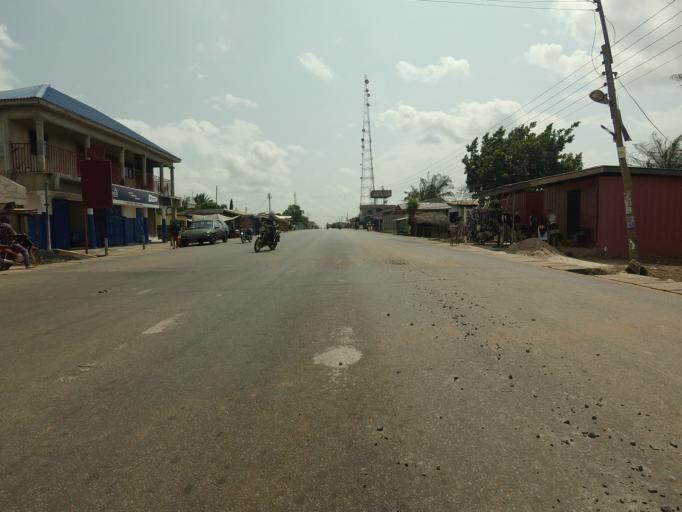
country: TG
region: Maritime
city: Lome
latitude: 6.2322
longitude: 1.0022
